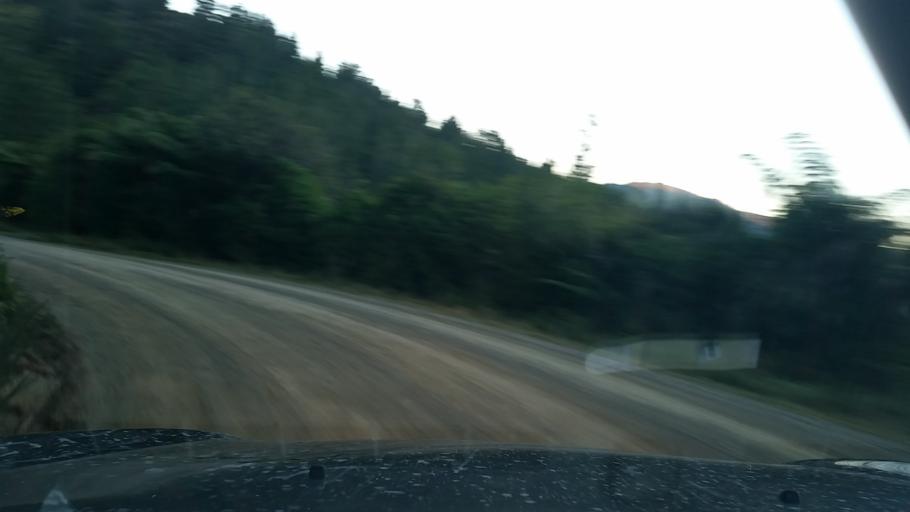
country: NZ
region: Marlborough
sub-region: Marlborough District
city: Picton
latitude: -41.1357
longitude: 174.1423
